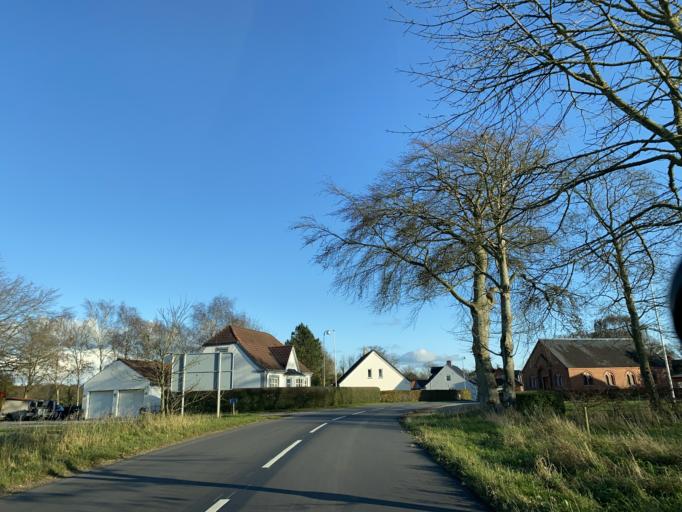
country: DK
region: Central Jutland
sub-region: Viborg Kommune
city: Bjerringbro
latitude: 56.3539
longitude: 9.6789
